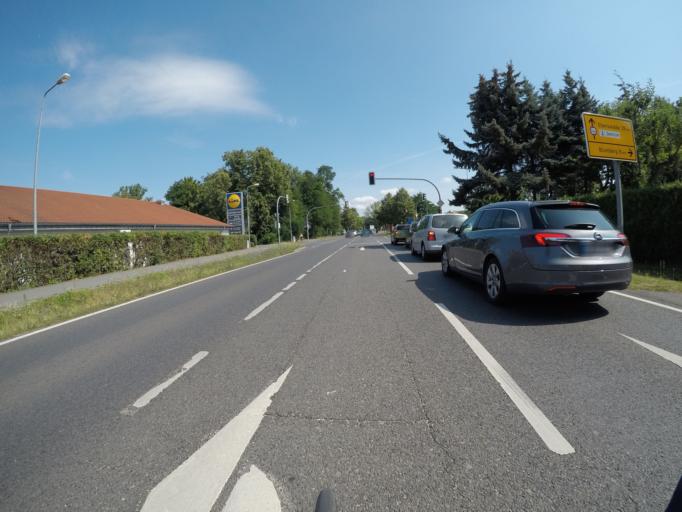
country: DE
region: Brandenburg
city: Bernau bei Berlin
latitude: 52.6690
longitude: 13.5825
